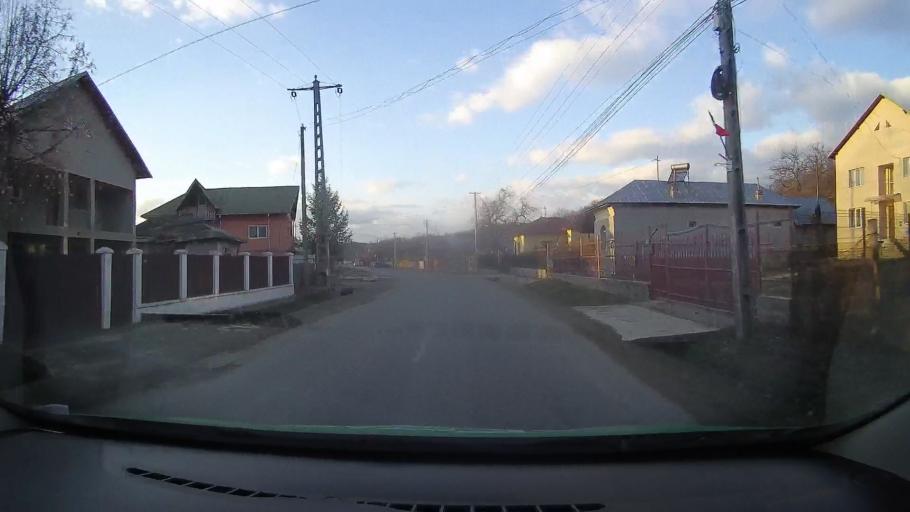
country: RO
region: Dambovita
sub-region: Comuna Gura Ocnitei
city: Adanca
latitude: 44.9279
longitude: 25.6037
